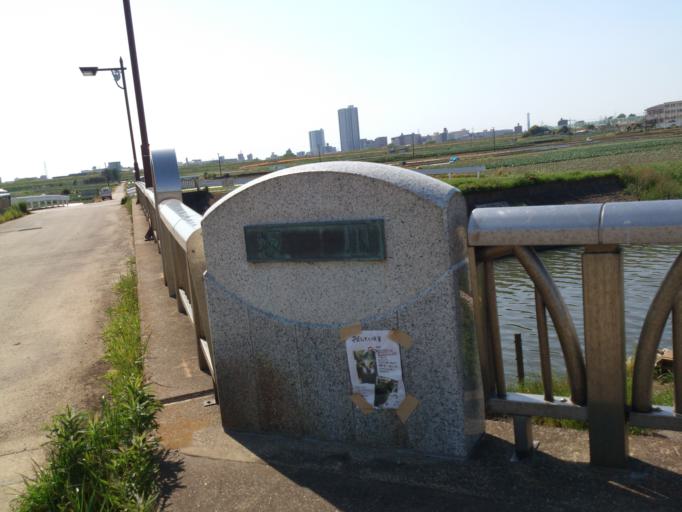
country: JP
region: Chiba
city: Matsudo
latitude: 35.7620
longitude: 139.8909
